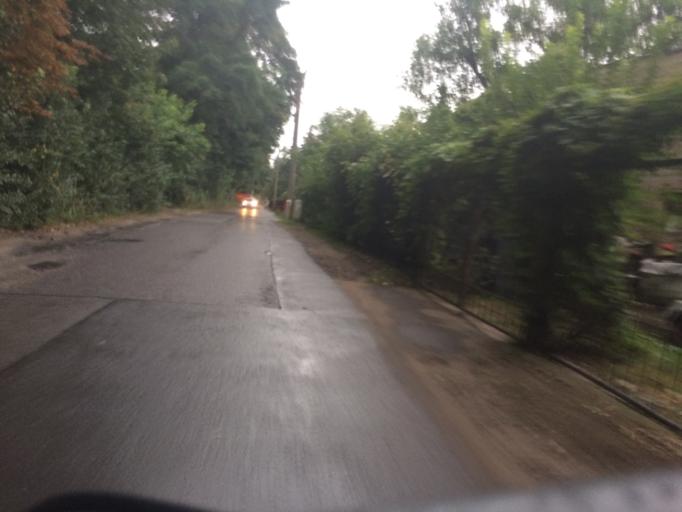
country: DE
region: Berlin
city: Wilhelmsruh
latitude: 52.5791
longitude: 13.3746
